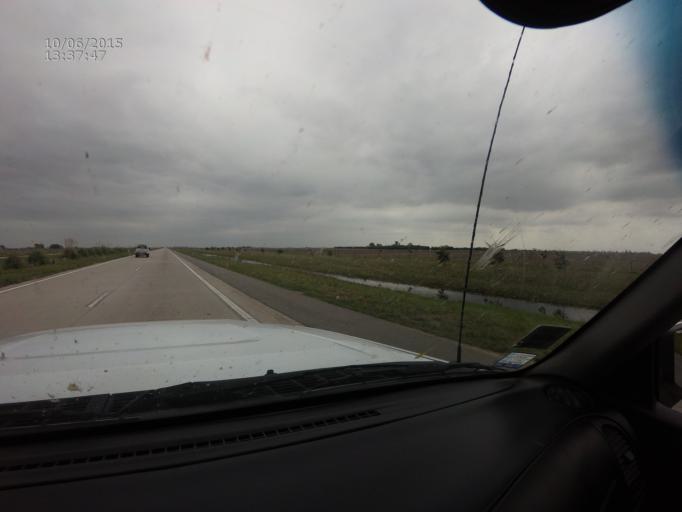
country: AR
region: Cordoba
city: Leones
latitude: -32.6068
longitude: -62.4212
